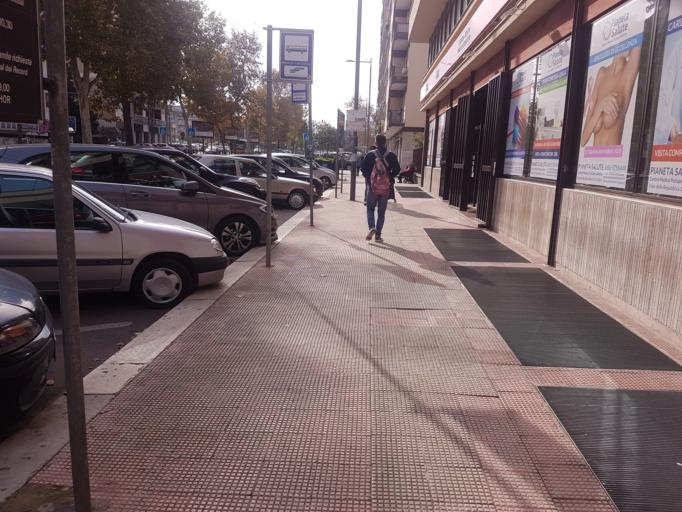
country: IT
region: Apulia
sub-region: Provincia di Bari
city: Bari
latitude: 41.1086
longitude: 16.8739
